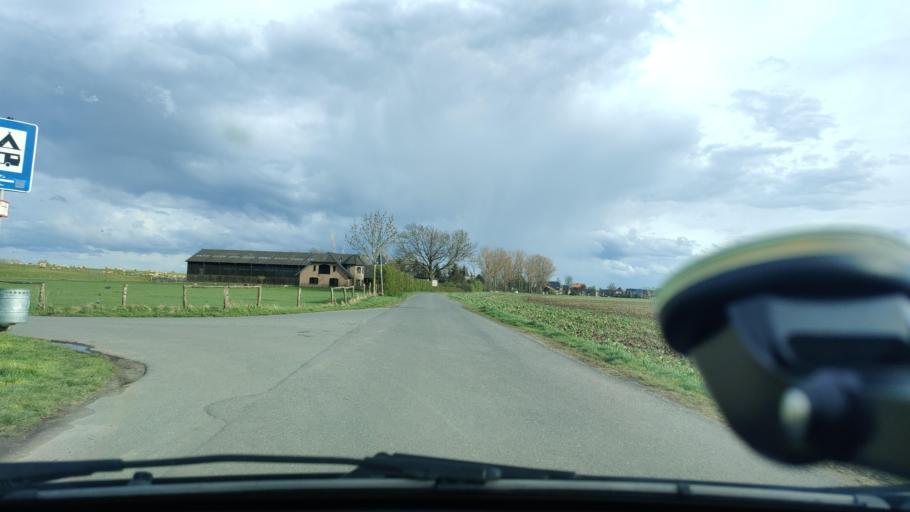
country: DE
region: North Rhine-Westphalia
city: Rees
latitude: 51.7375
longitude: 6.4074
